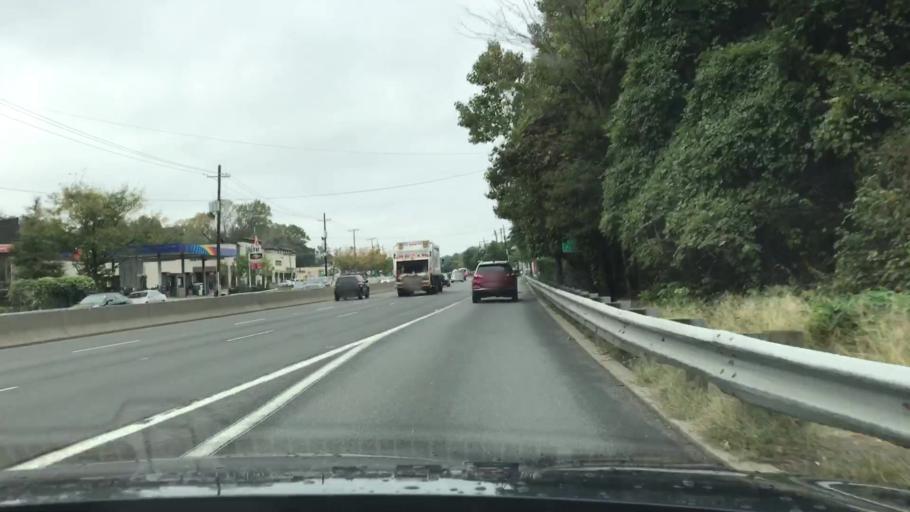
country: US
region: New Jersey
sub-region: Bergen County
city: River Edge
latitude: 40.9124
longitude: -74.0413
